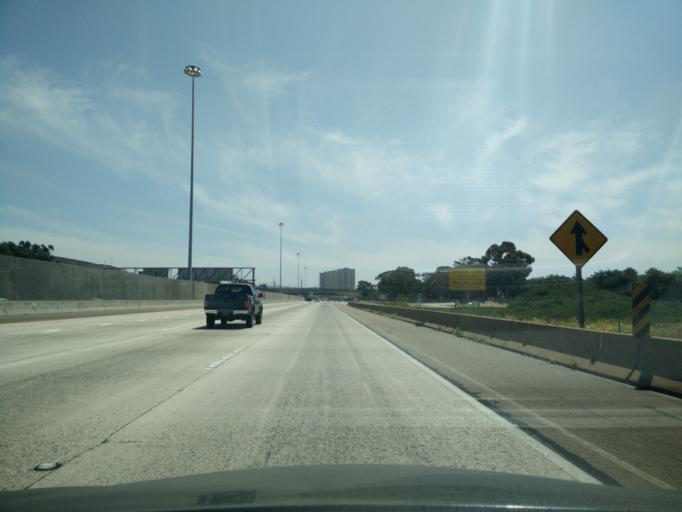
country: MX
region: Baja California
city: Tijuana
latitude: 32.5472
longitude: -117.0371
